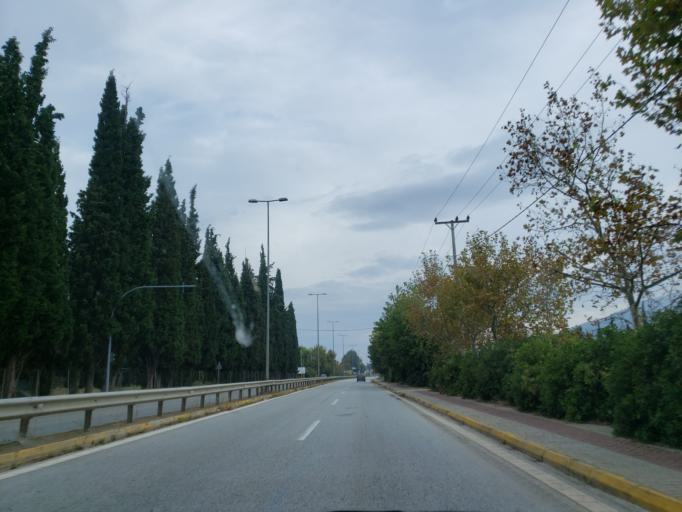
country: GR
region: Attica
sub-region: Nomarchia Anatolikis Attikis
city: Marathonas
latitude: 38.1354
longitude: 23.9672
